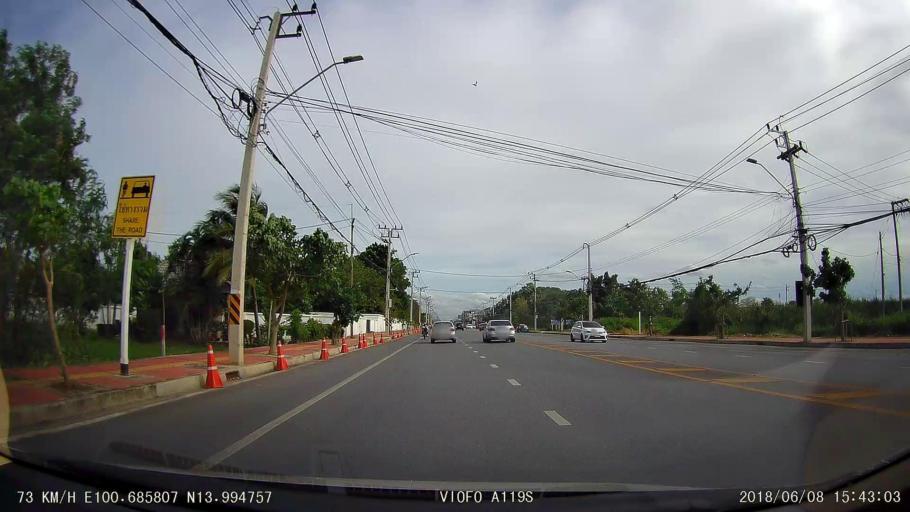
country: TH
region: Pathum Thani
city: Thanyaburi
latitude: 13.9945
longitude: 100.6858
